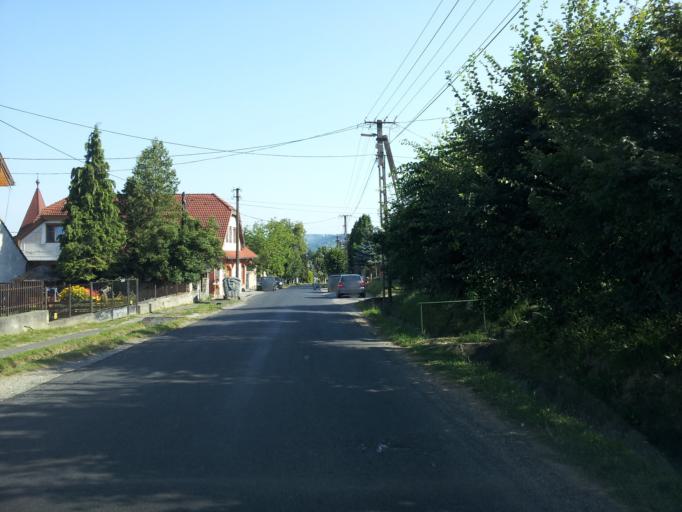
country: HU
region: Zala
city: Gyenesdias
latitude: 46.8628
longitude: 17.2980
